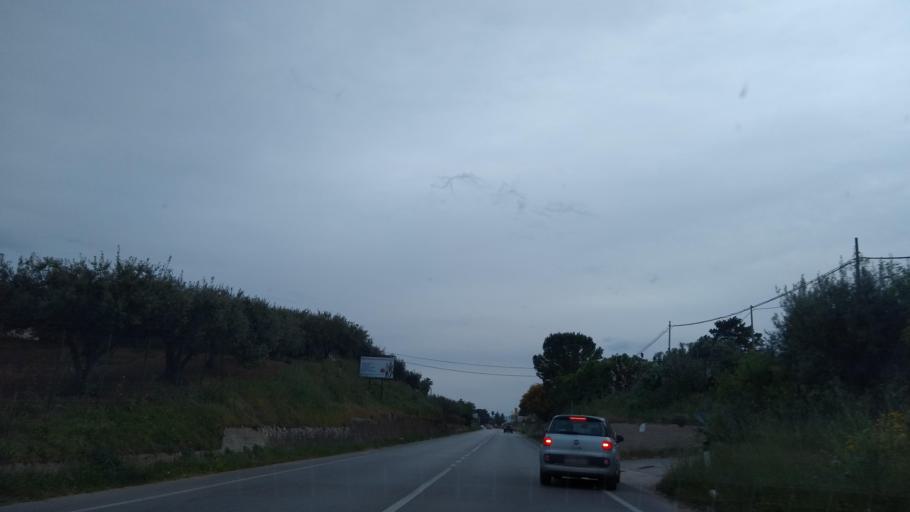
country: IT
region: Sicily
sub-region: Palermo
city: Partinico
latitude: 38.0356
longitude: 13.1011
